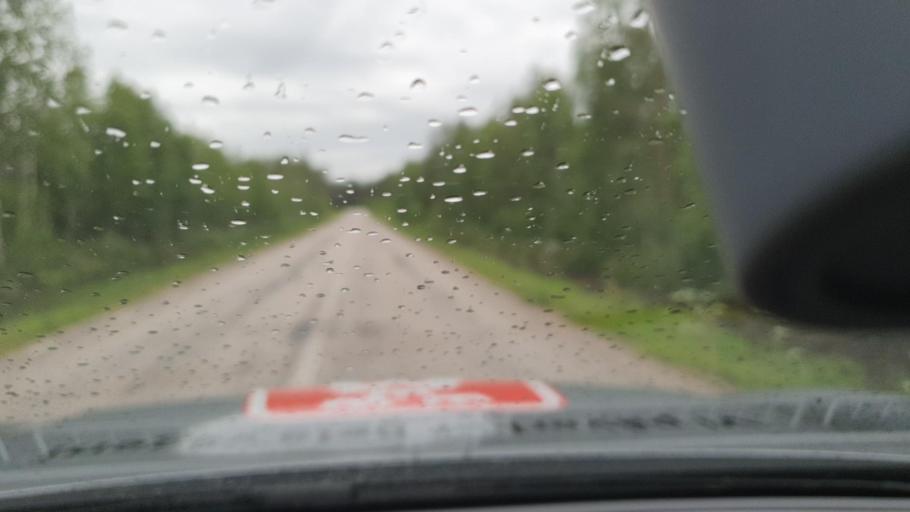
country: SE
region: Norrbotten
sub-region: Overkalix Kommun
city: OEverkalix
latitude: 66.3607
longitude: 22.8022
